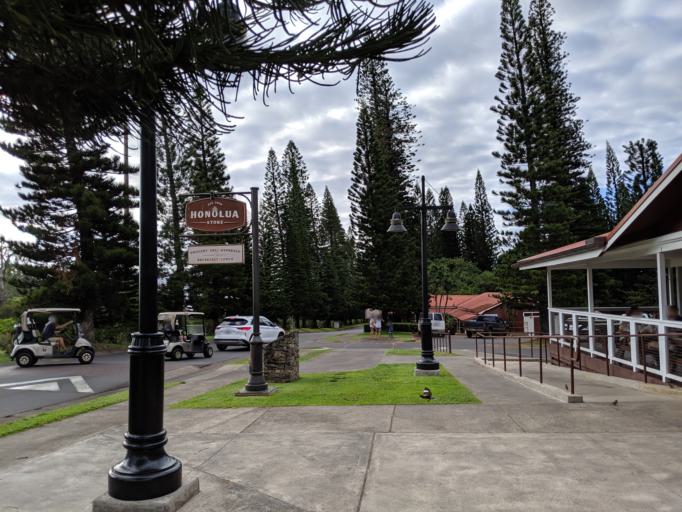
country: US
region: Hawaii
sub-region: Maui County
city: Napili-Honokowai
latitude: 20.9987
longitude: -156.6546
